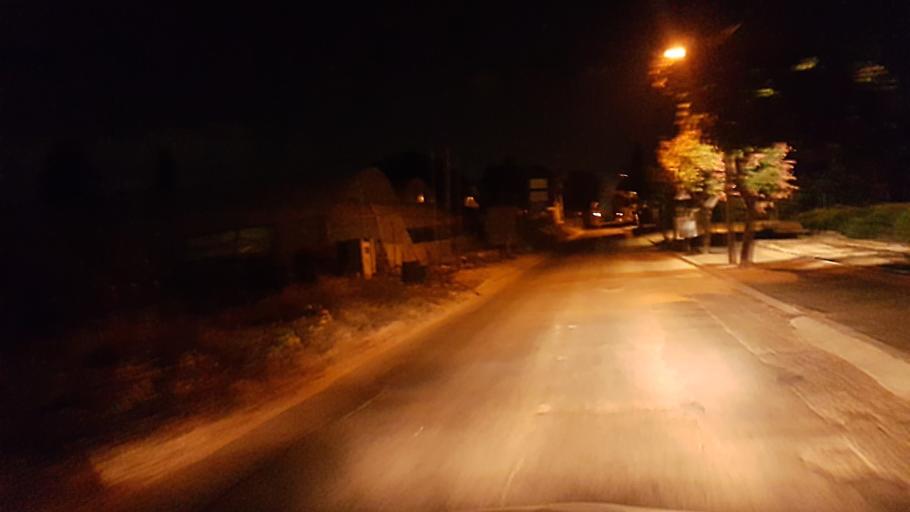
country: IL
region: Central District
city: Hod HaSharon
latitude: 32.1631
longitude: 34.8745
